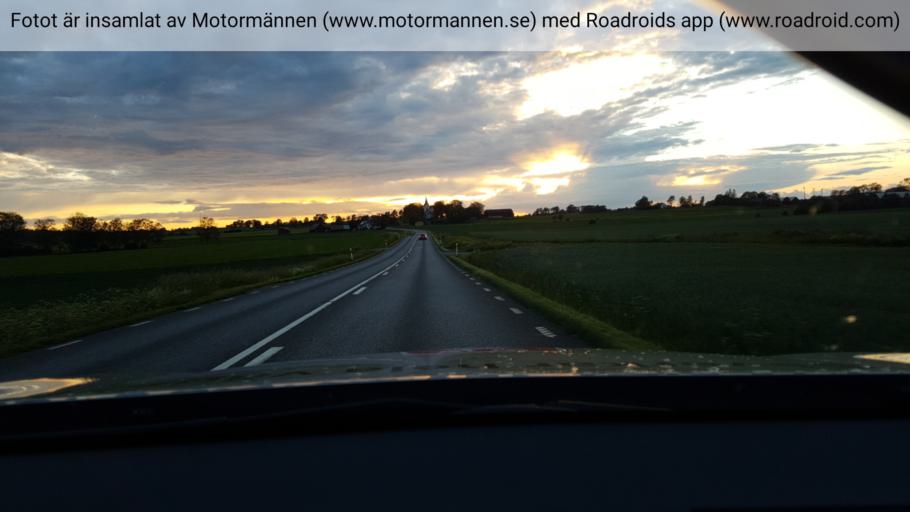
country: SE
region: Joenkoeping
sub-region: Mullsjo Kommun
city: Mullsjoe
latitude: 58.0775
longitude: 13.7908
